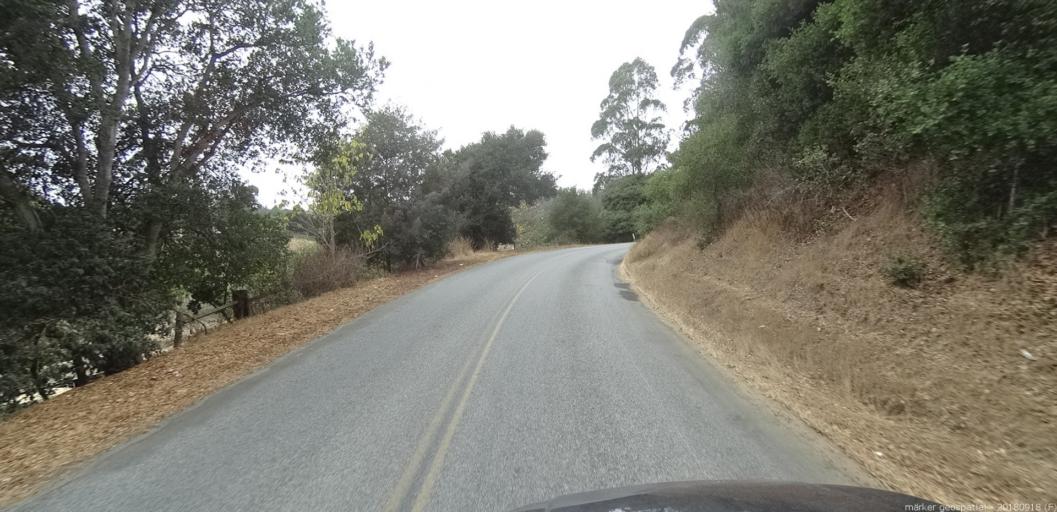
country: US
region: California
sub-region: Monterey County
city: Prunedale
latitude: 36.7759
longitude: -121.6593
